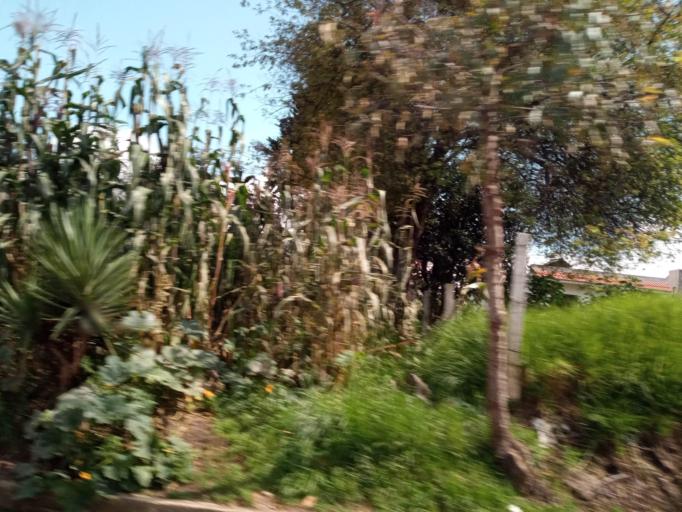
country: GT
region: Quetzaltenango
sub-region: Municipio de La Esperanza
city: La Esperanza
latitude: 14.8554
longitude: -91.5446
